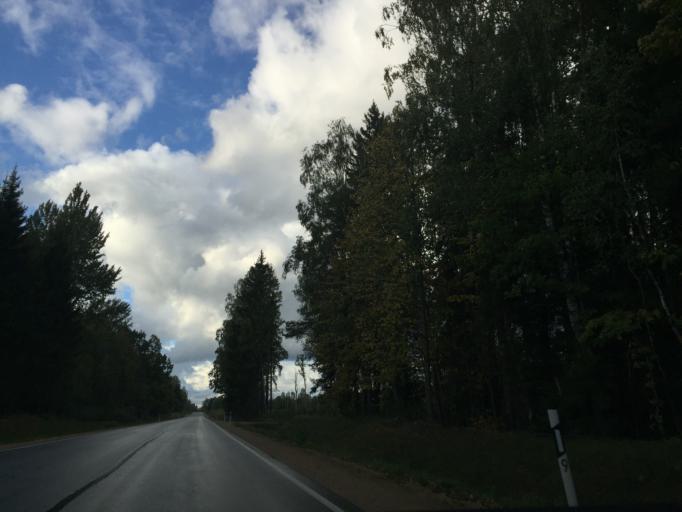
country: LV
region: Ligatne
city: Ligatne
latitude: 57.1668
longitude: 25.0476
